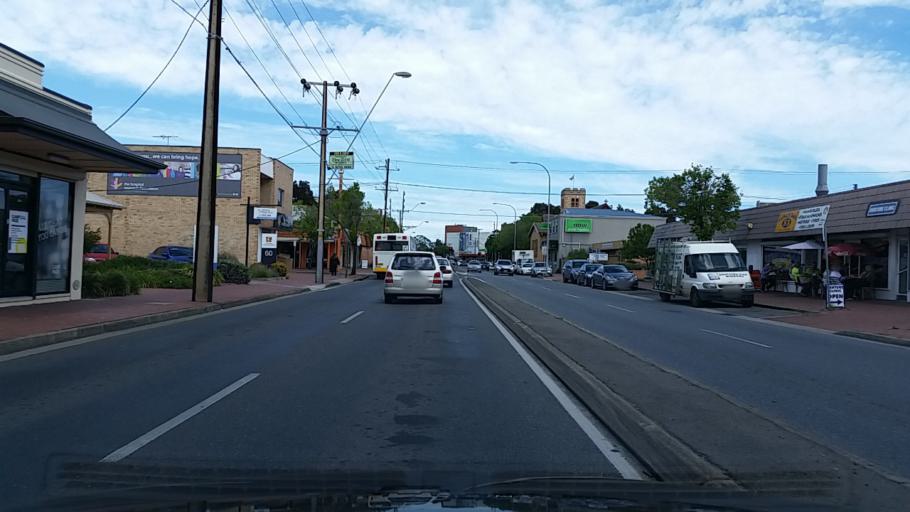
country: AU
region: South Australia
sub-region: Charles Sturt
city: Woodville West
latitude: -34.8793
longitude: 138.5365
